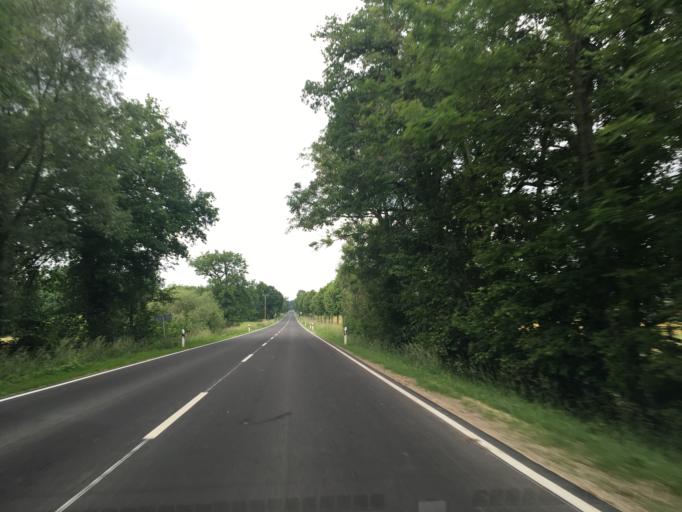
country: DE
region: North Rhine-Westphalia
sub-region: Regierungsbezirk Munster
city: Horstmar
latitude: 52.1033
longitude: 7.3287
